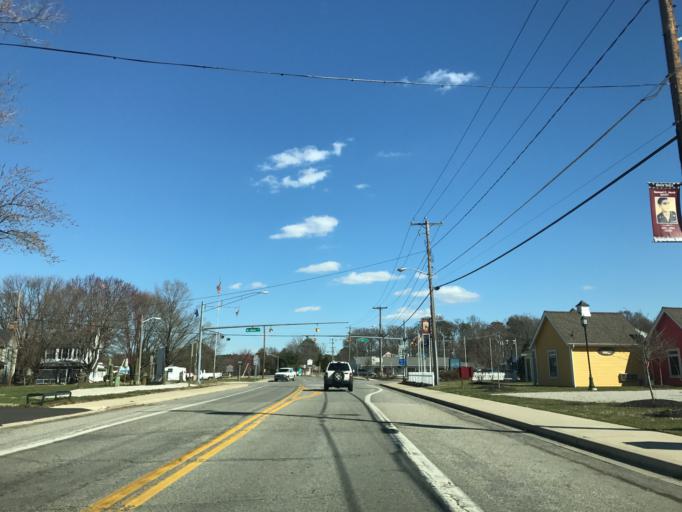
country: US
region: Maryland
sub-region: Kent County
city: Rock Hall
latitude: 39.1386
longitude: -76.2358
